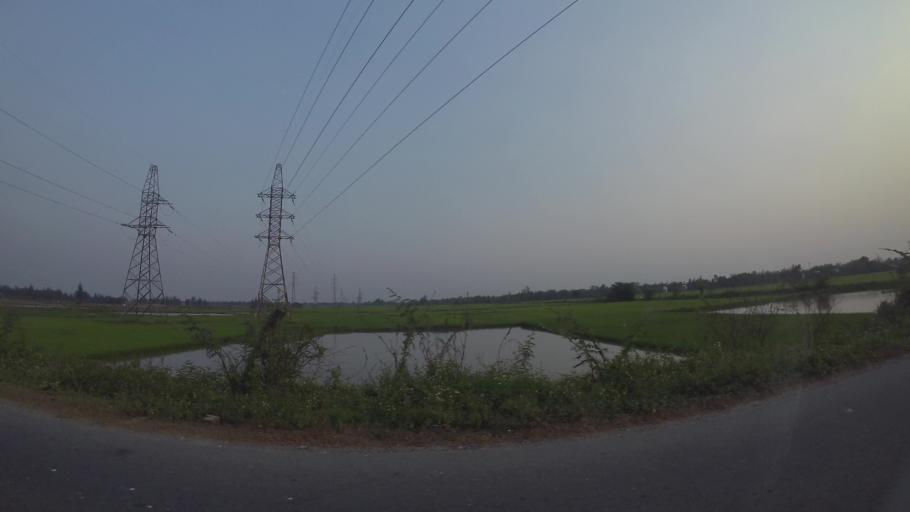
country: VN
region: Da Nang
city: Ngu Hanh Son
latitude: 15.9534
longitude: 108.2372
